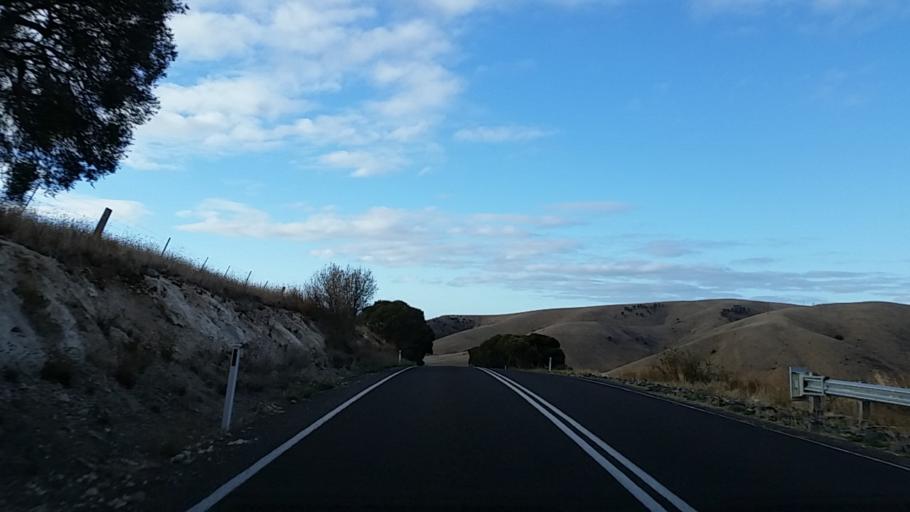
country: AU
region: South Australia
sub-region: Yankalilla
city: Normanville
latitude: -35.5430
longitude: 138.1939
